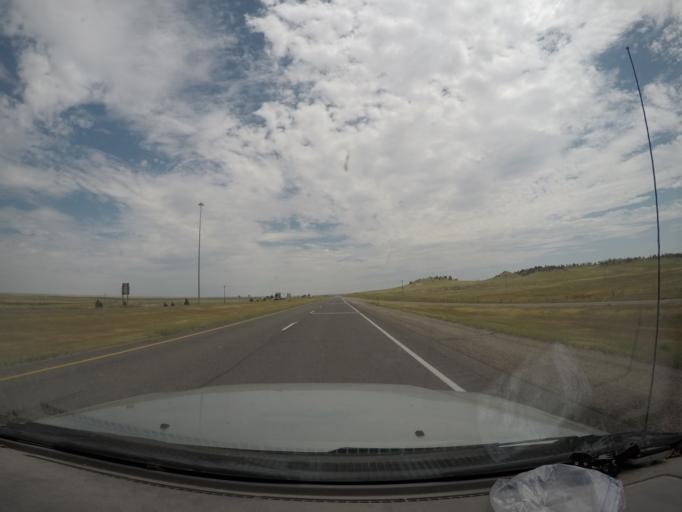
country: US
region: Wyoming
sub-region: Laramie County
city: Pine Bluffs
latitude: 41.1835
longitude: -104.0411
